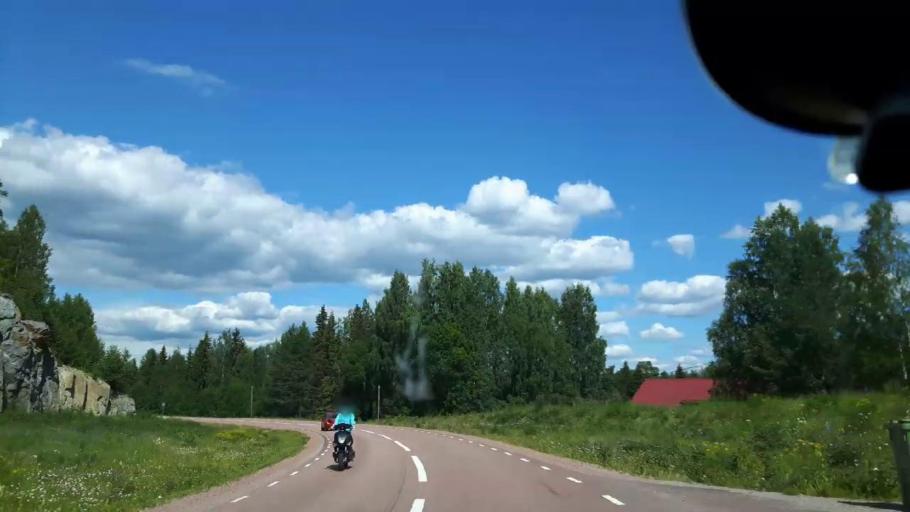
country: SE
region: Jaemtland
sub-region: Ragunda Kommun
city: Hammarstrand
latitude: 63.0377
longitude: 16.5191
